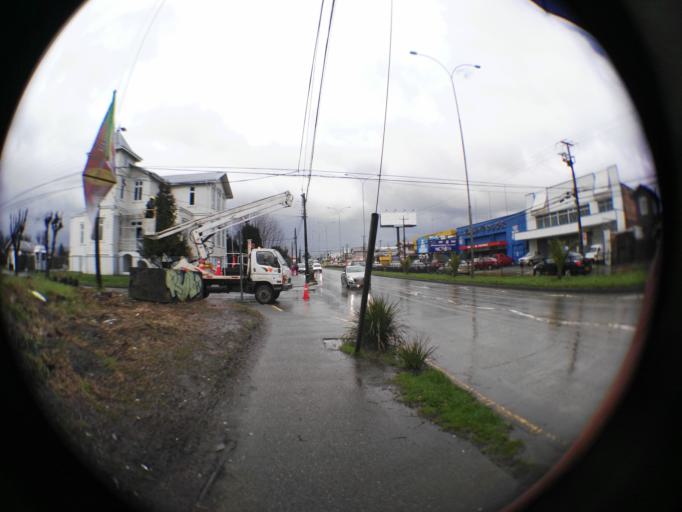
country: CL
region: Los Lagos
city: Las Animas
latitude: -39.8268
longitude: -73.2237
